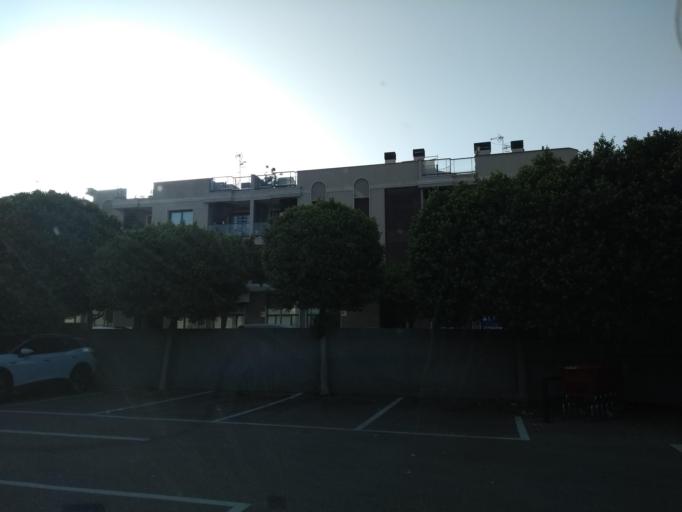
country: ES
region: Balearic Islands
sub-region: Illes Balears
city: Inca
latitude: 39.7261
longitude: 2.9205
